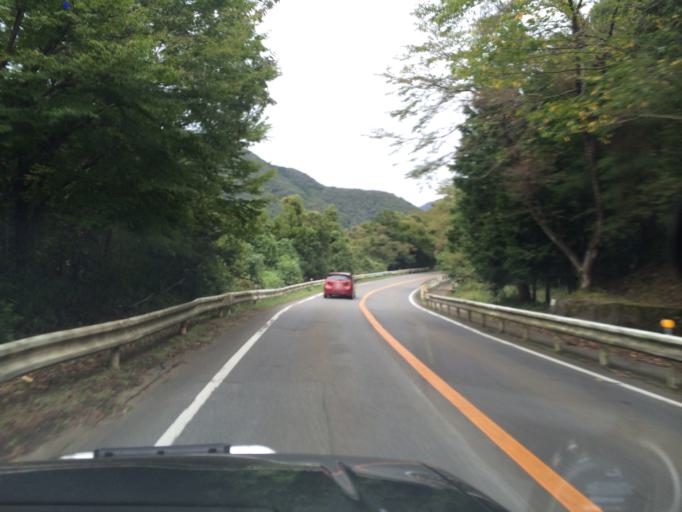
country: JP
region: Hyogo
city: Toyooka
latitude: 35.4091
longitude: 134.7809
